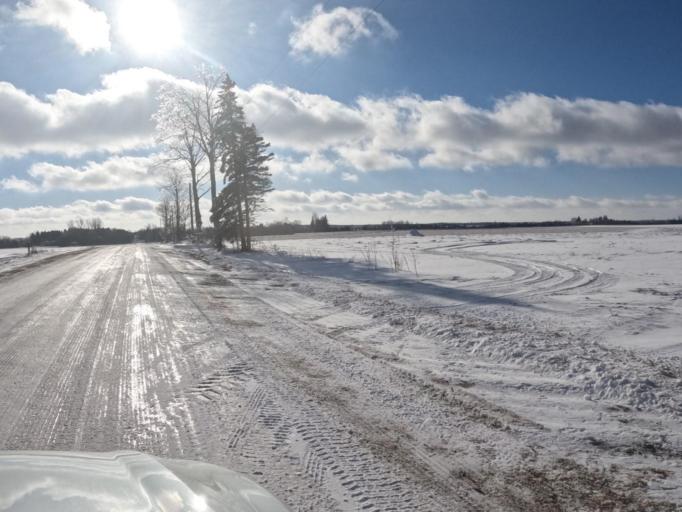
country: CA
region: Ontario
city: Shelburne
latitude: 43.9877
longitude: -80.4068
